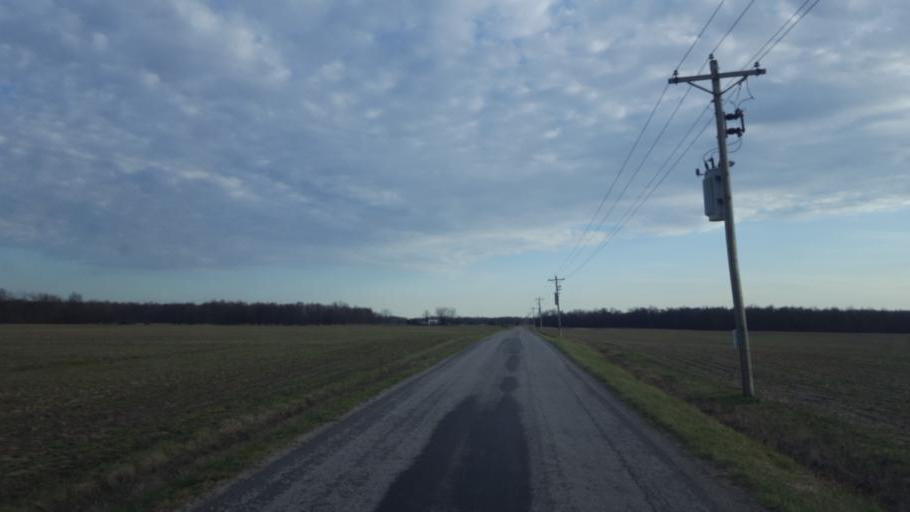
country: US
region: Ohio
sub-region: Marion County
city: Marion
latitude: 40.6156
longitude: -82.9910
